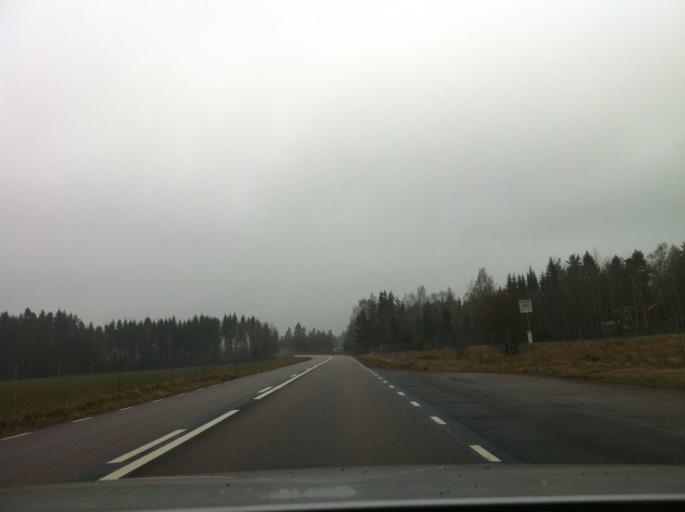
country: SE
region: Vaestra Goetaland
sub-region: Vanersborgs Kommun
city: Bralanda
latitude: 58.5098
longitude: 12.2177
